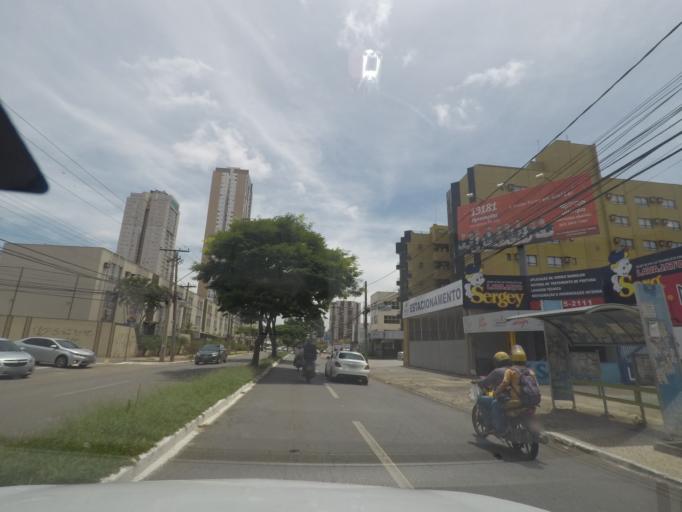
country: BR
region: Goias
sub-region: Goiania
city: Goiania
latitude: -16.6912
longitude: -49.2650
